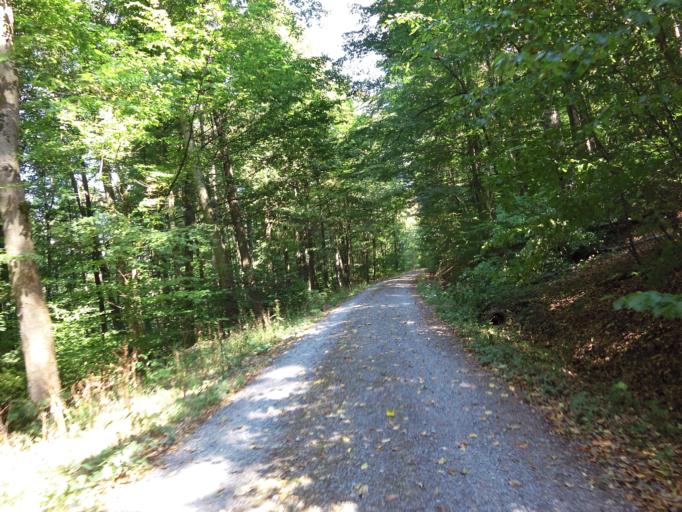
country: DE
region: Bavaria
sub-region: Regierungsbezirk Unterfranken
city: Wuerzburg
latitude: 49.7605
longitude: 9.8921
